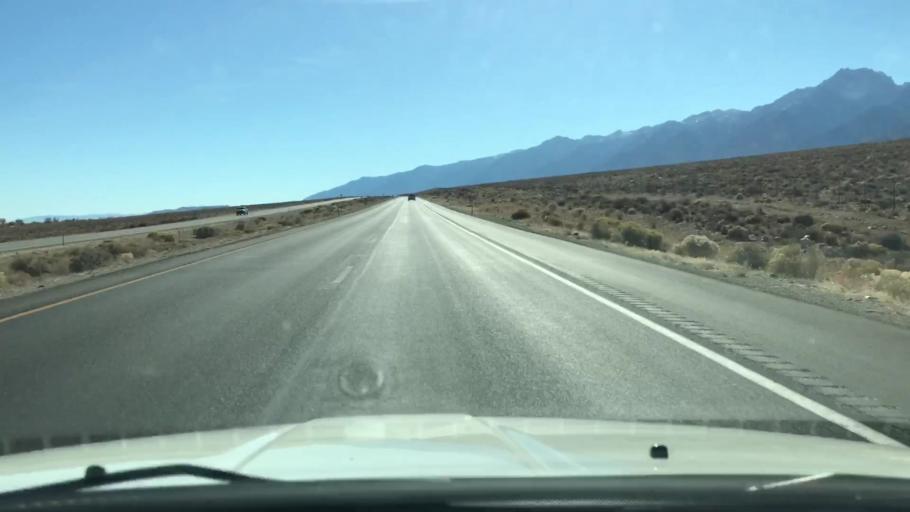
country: US
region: California
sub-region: Inyo County
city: Big Pine
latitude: 36.8630
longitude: -118.2354
